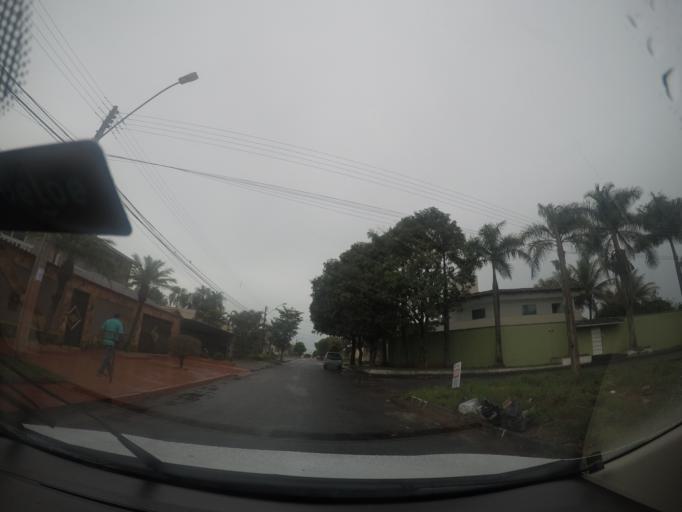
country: BR
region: Goias
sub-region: Goiania
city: Goiania
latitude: -16.6337
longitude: -49.2309
